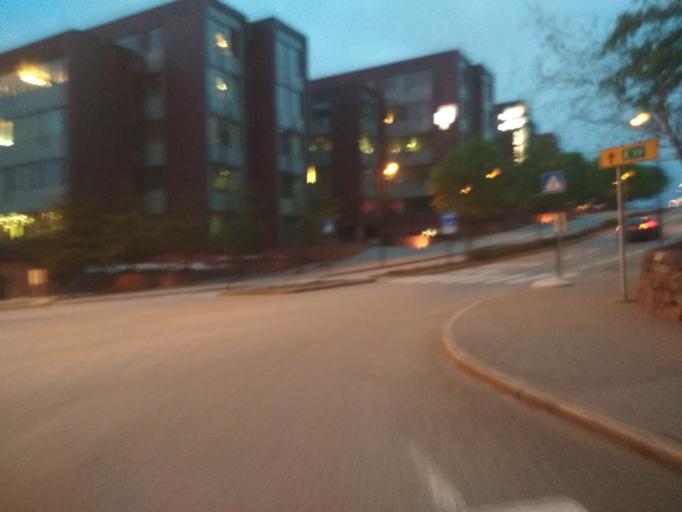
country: NO
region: Rogaland
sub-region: Stavanger
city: Stavanger
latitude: 58.9739
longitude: 5.7213
